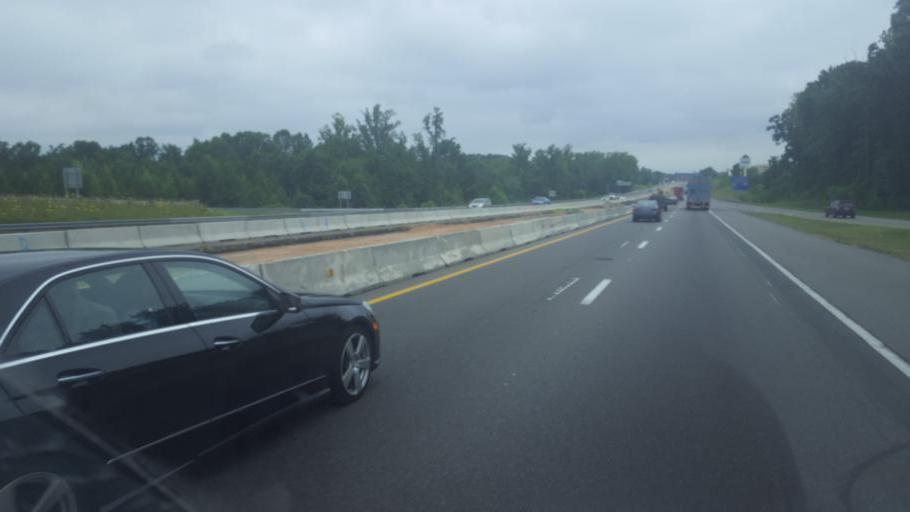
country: US
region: North Carolina
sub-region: Iredell County
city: Mooresville
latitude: 35.5817
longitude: -80.8566
